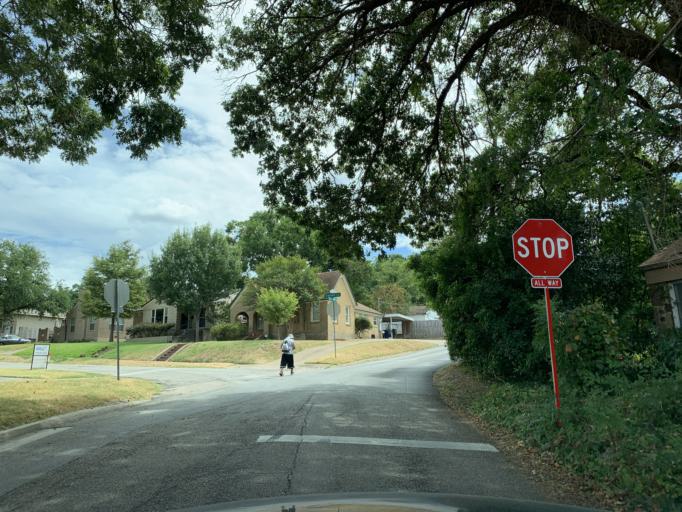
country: US
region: Texas
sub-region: Dallas County
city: Cockrell Hill
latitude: 32.7400
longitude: -96.8762
